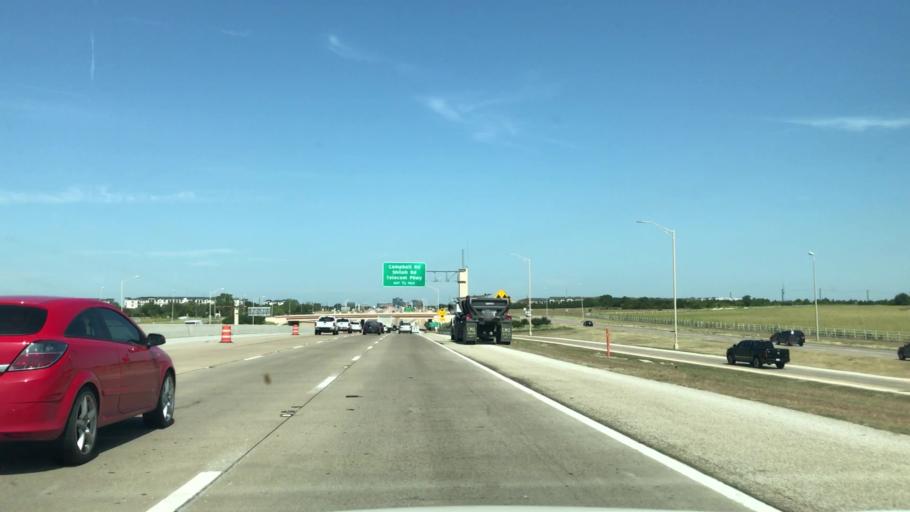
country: US
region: Texas
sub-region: Dallas County
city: Sachse
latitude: 32.9681
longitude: -96.6448
